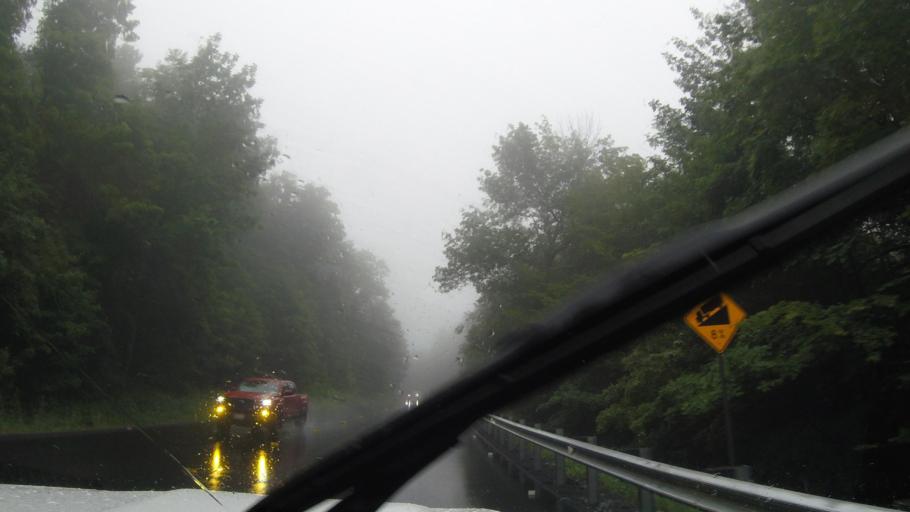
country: US
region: Vermont
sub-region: Windham County
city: Dover
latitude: 42.8559
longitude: -72.7908
